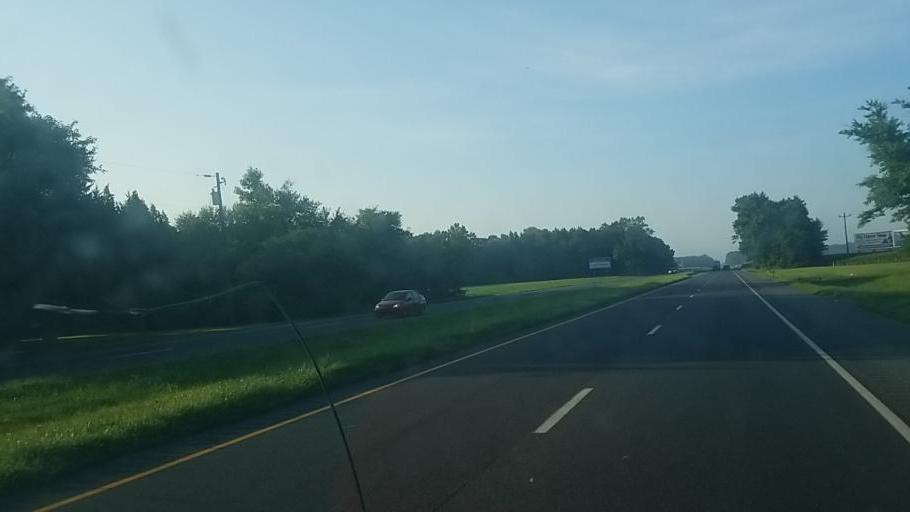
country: US
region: Delaware
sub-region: Sussex County
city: Selbyville
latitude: 38.4997
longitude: -75.2373
